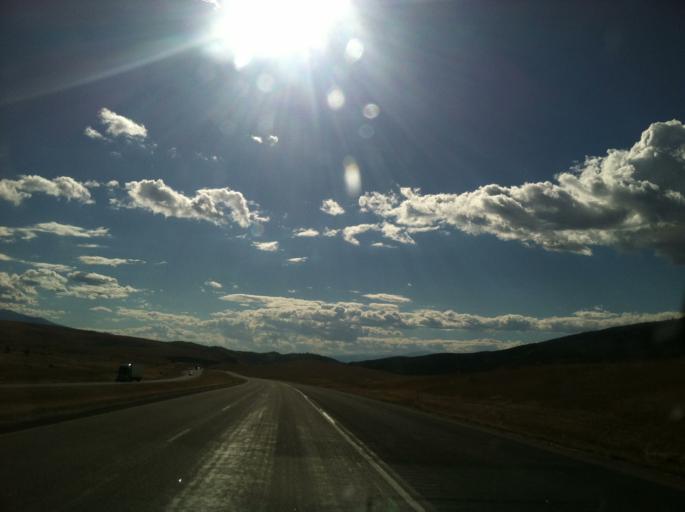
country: US
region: Montana
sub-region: Jefferson County
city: Whitehall
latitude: 45.8887
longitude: -111.8608
